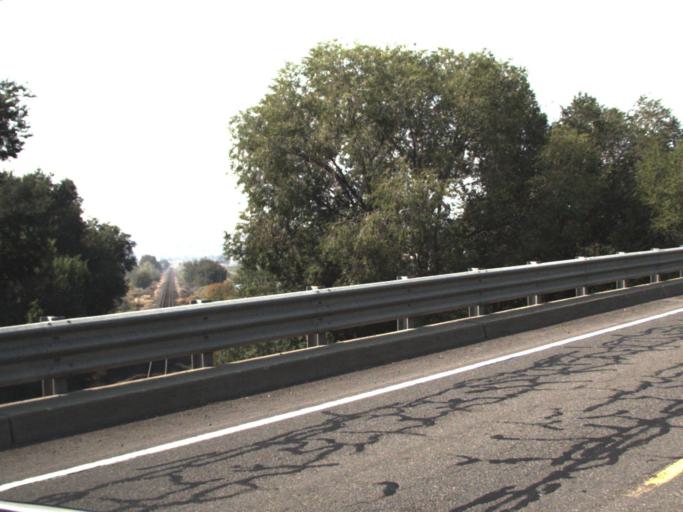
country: US
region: Washington
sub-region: Yakima County
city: Selah
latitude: 46.6793
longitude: -120.4979
